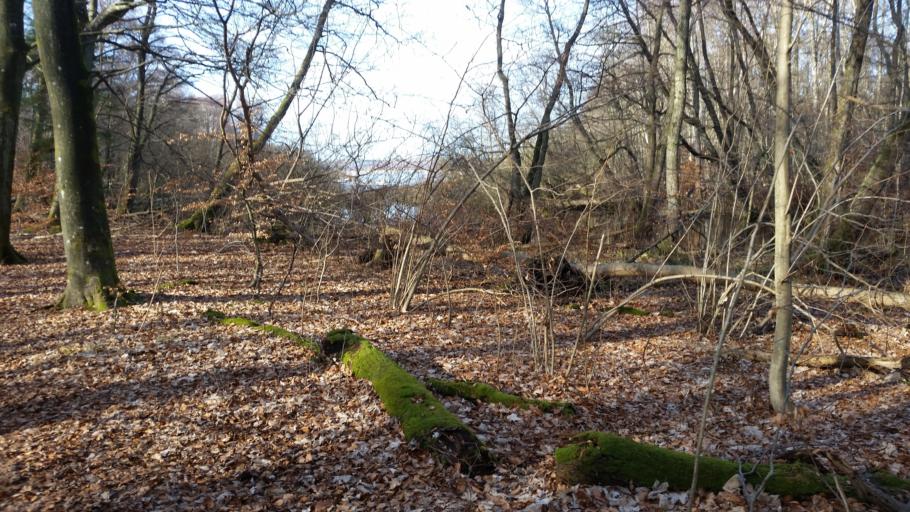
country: DK
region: Capital Region
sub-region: Fredensborg Kommune
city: Humlebaek
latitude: 56.0224
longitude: 12.4962
